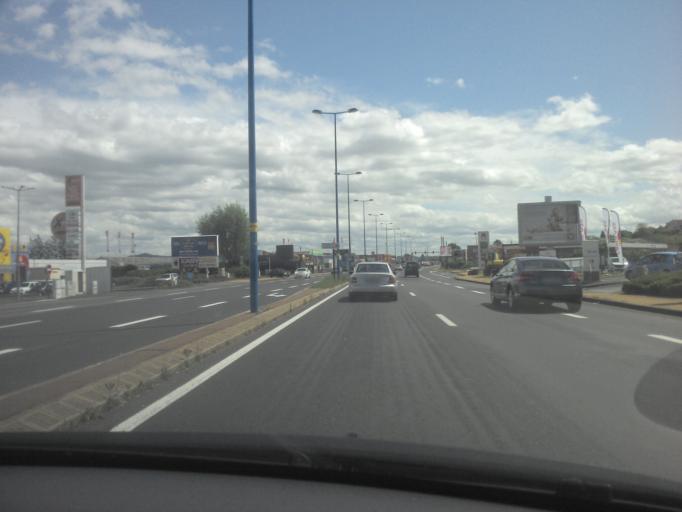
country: FR
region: Auvergne
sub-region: Departement du Puy-de-Dome
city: Aubiere
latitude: 45.7551
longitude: 3.1295
